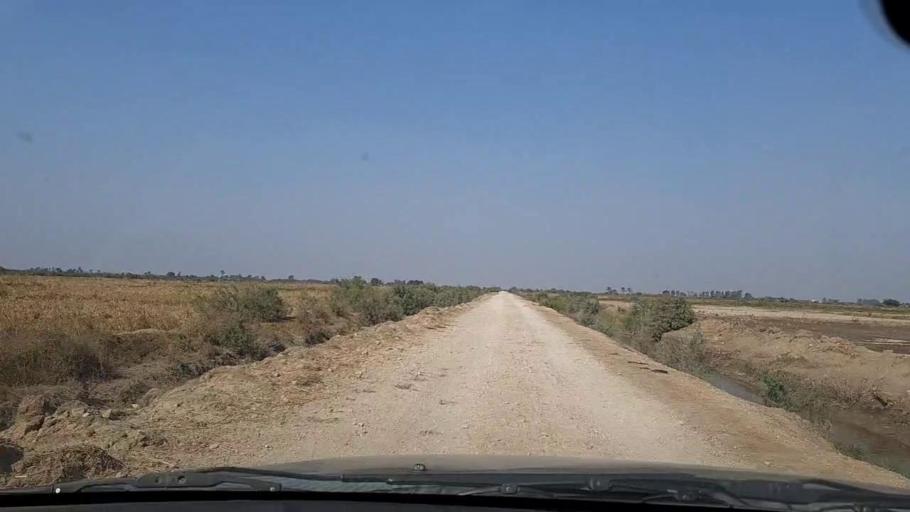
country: PK
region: Sindh
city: Mirpur Sakro
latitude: 24.3688
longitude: 67.6830
